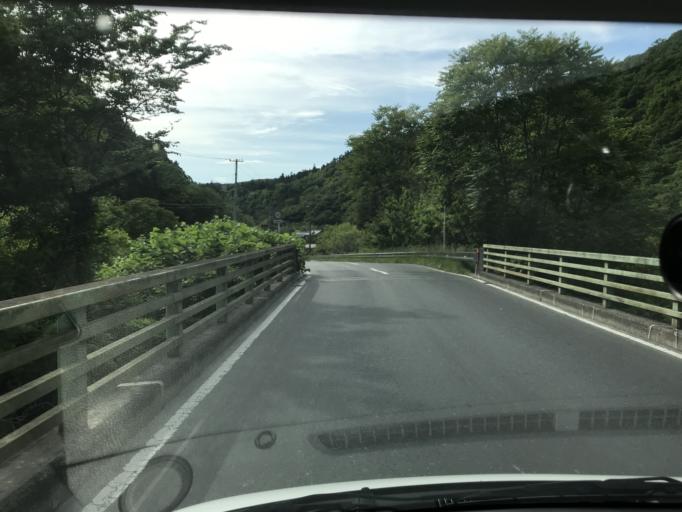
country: JP
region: Miyagi
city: Wakuya
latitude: 38.6581
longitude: 141.3152
